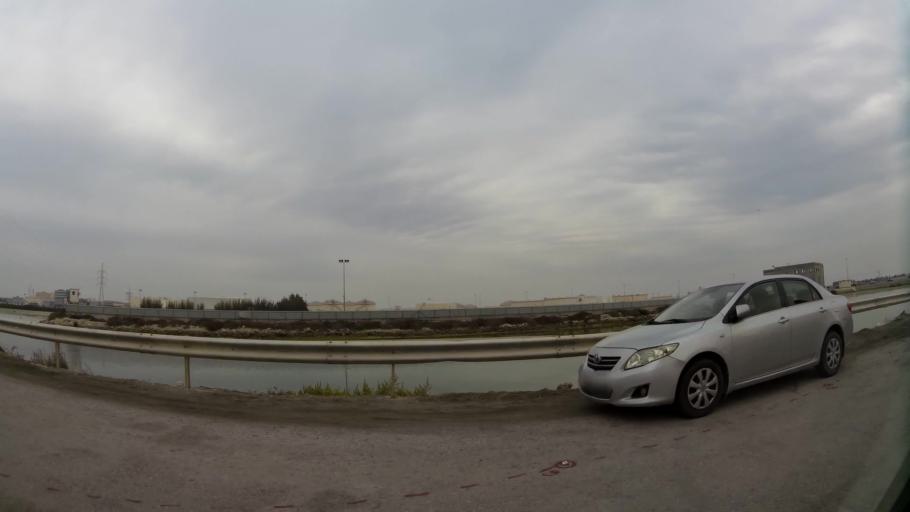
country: BH
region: Northern
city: Sitrah
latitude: 26.1441
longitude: 50.6152
